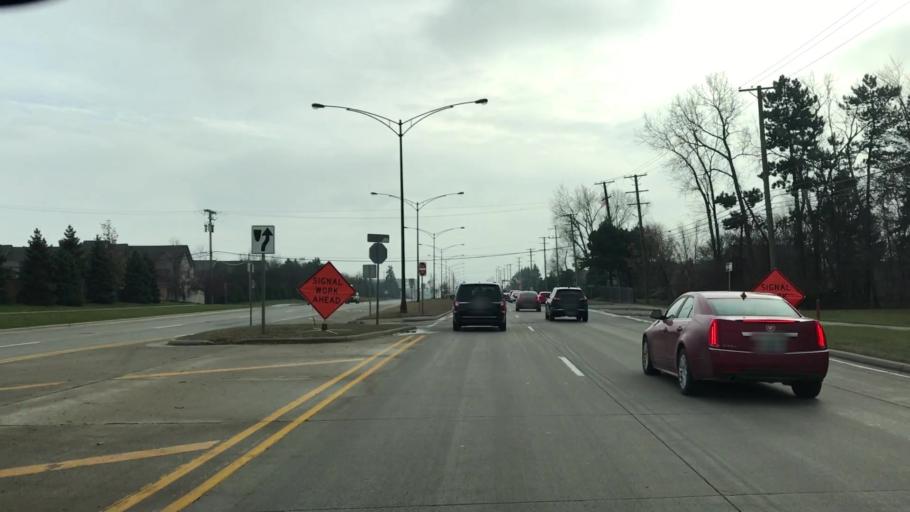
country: US
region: Michigan
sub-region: Oakland County
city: Troy
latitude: 42.5824
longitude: -83.1287
